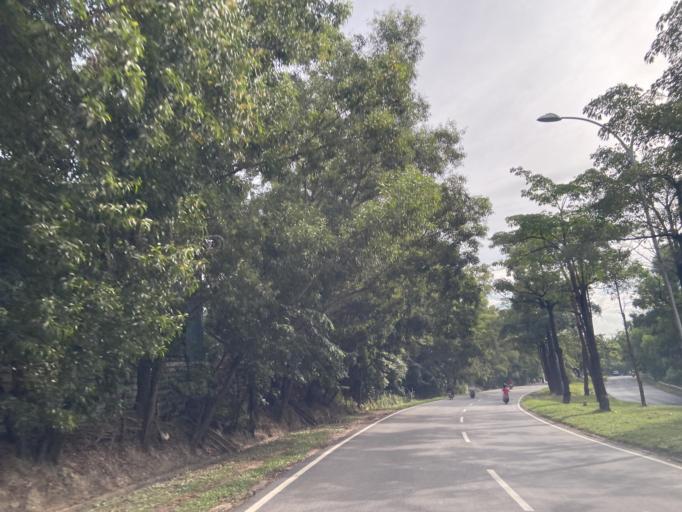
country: SG
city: Singapore
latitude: 1.1455
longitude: 104.0215
